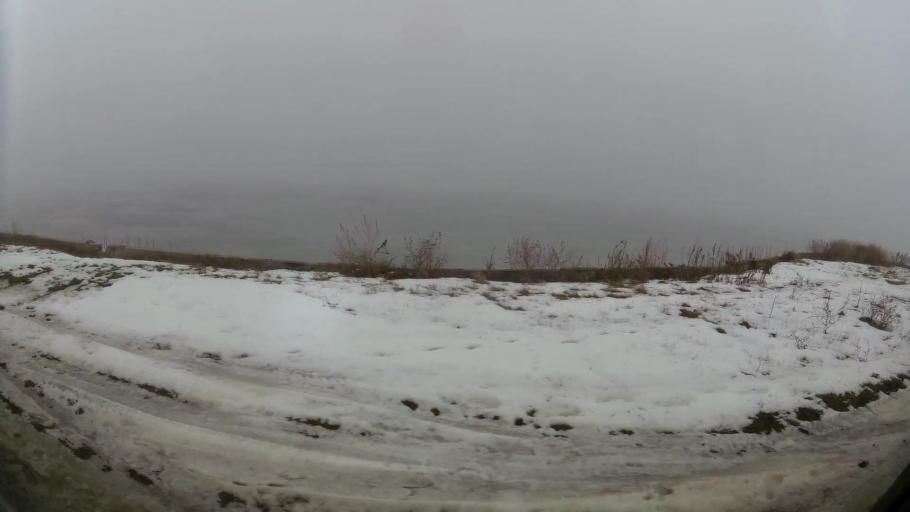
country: RO
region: Ilfov
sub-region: Comuna Chiajna
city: Rosu
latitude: 44.4508
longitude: 26.0278
